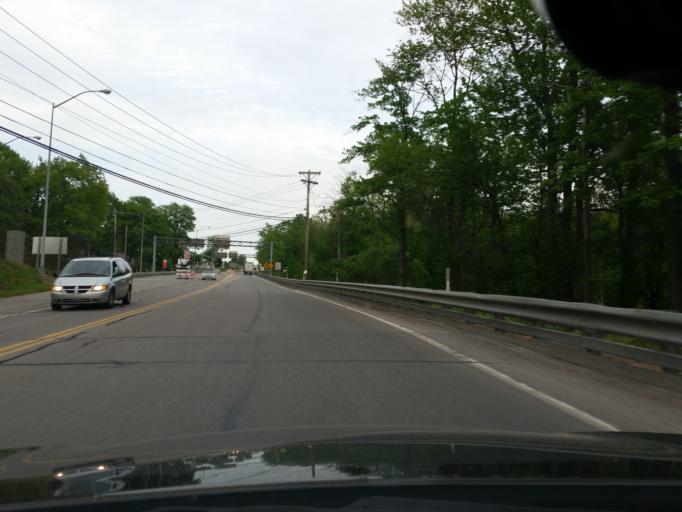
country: US
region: Pennsylvania
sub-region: Elk County
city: Ridgway
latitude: 41.4122
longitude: -78.7139
